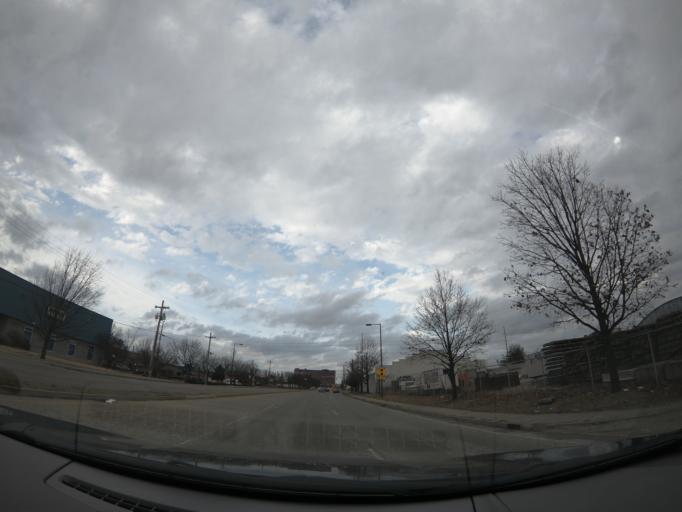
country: US
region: Kentucky
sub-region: Jefferson County
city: Louisville
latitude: 38.2391
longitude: -85.7680
